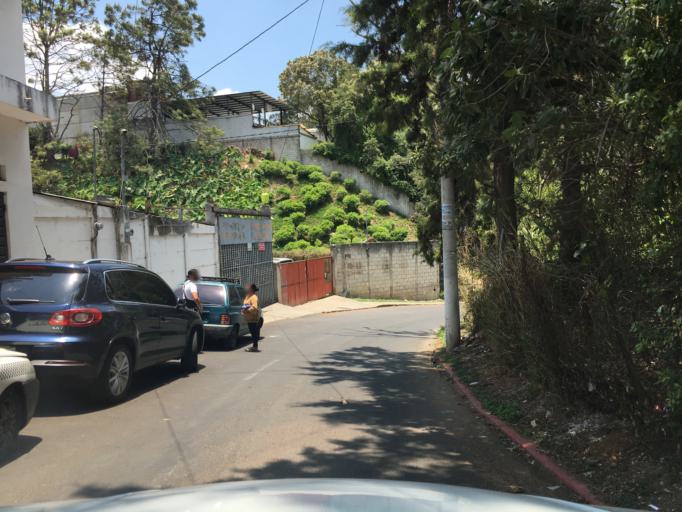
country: GT
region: Guatemala
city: Guatemala City
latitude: 14.6108
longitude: -90.5027
